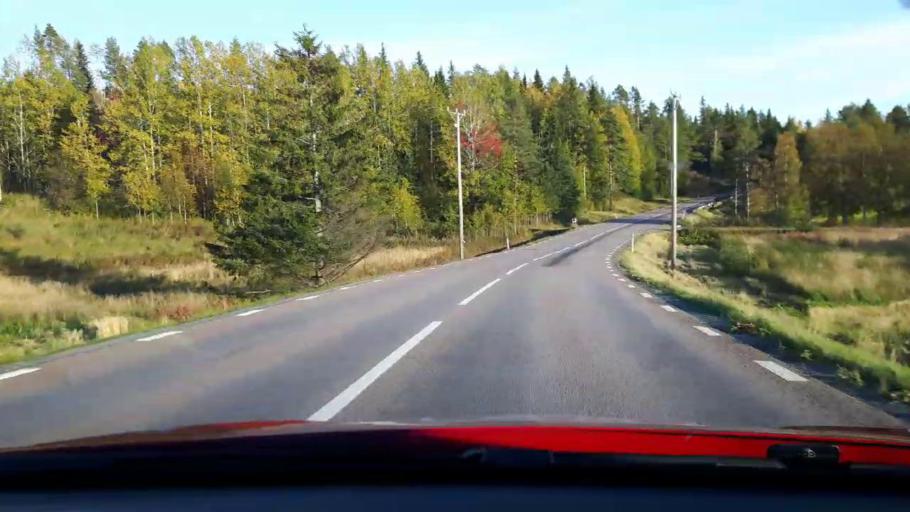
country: SE
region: Jaemtland
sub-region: OEstersunds Kommun
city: Brunflo
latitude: 63.0174
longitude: 14.9468
